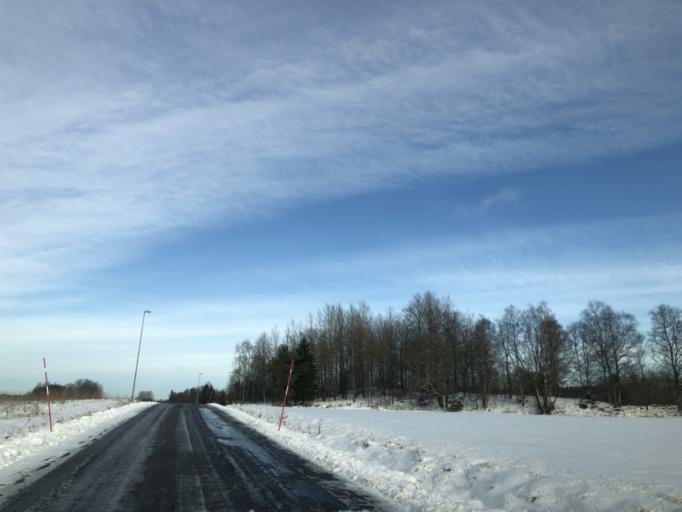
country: SE
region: Vaestra Goetaland
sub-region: Ulricehamns Kommun
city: Ulricehamn
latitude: 57.7905
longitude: 13.5301
